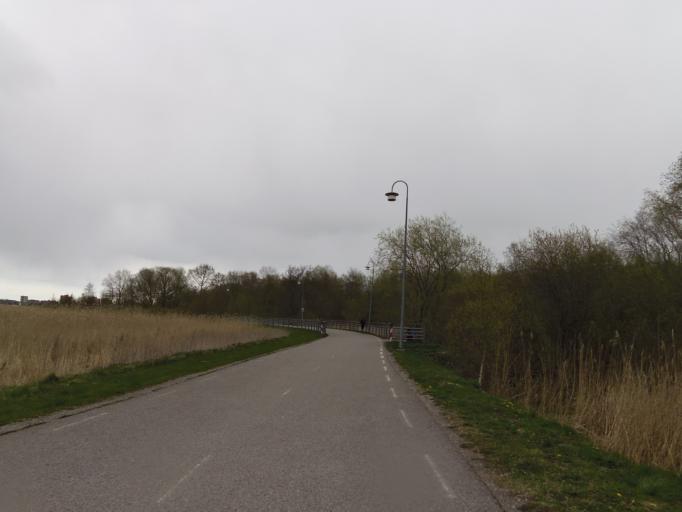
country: EE
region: Harju
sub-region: Tallinna linn
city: Tallinn
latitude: 59.4292
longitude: 24.6709
